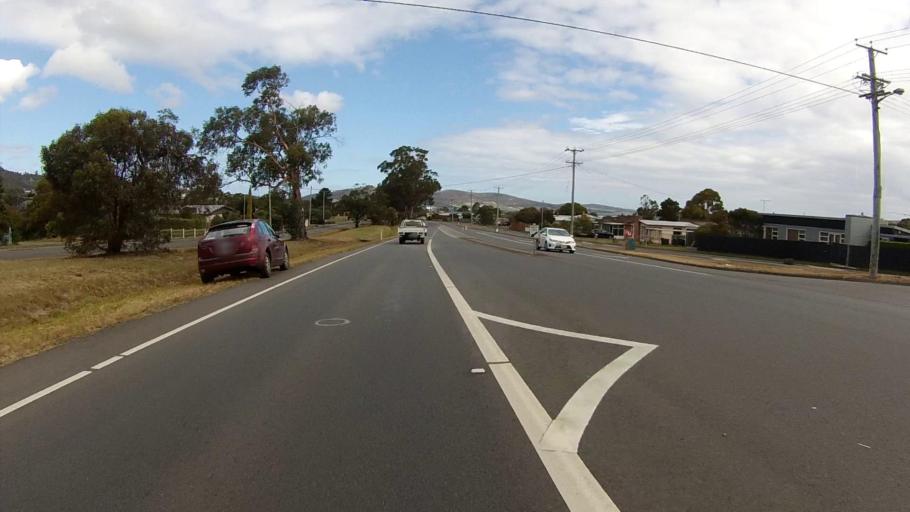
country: AU
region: Tasmania
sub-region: Clarence
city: Rokeby
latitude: -42.8942
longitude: 147.4373
